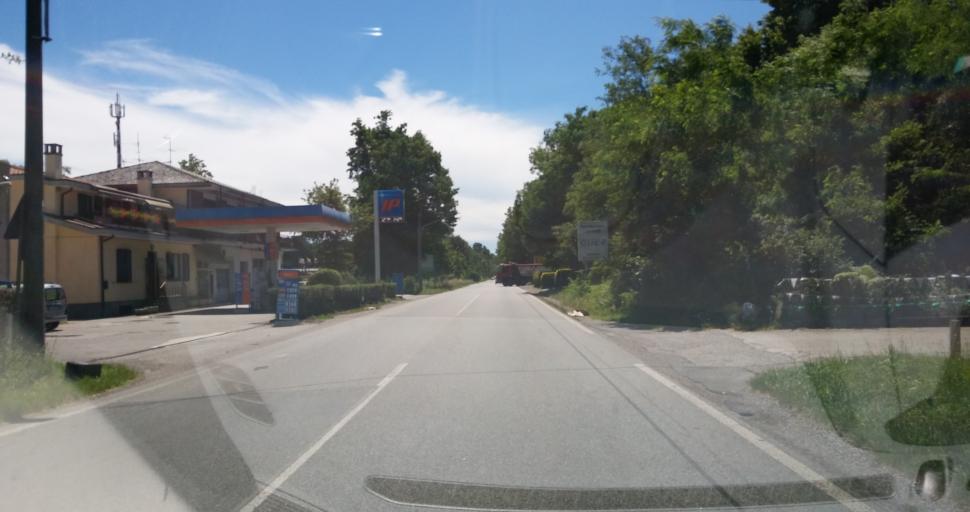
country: IT
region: Lombardy
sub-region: Provincia di Varese
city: Vergiate
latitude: 45.7125
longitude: 8.6943
